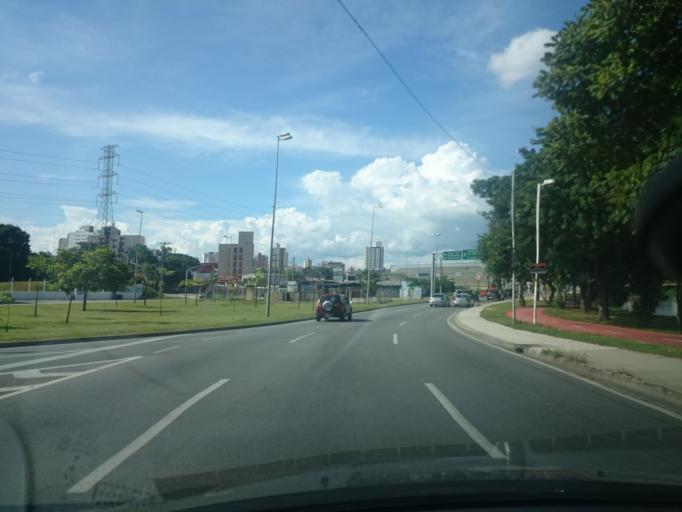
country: BR
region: Sao Paulo
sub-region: Sorocaba
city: Sorocaba
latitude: -23.5108
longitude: -47.4529
